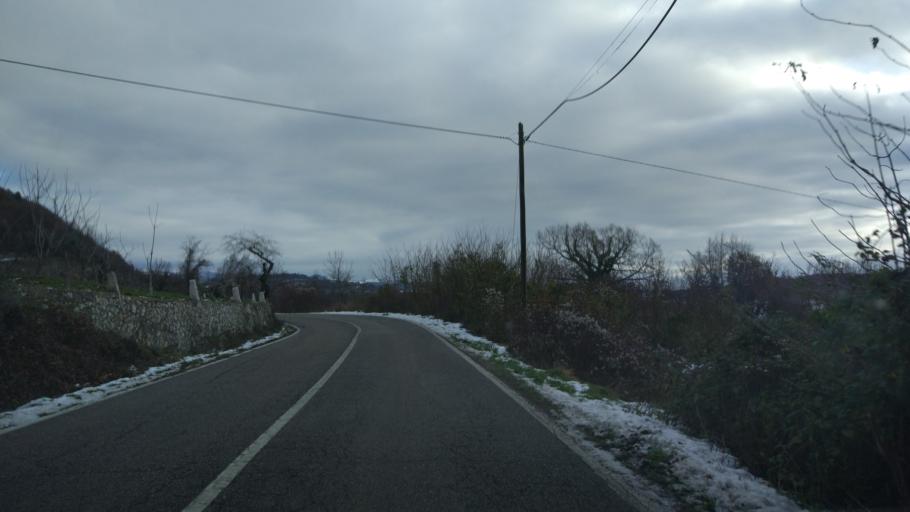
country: IT
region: Veneto
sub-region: Provincia di Verona
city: Marano di Valpolicella
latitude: 45.5734
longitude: 10.9262
